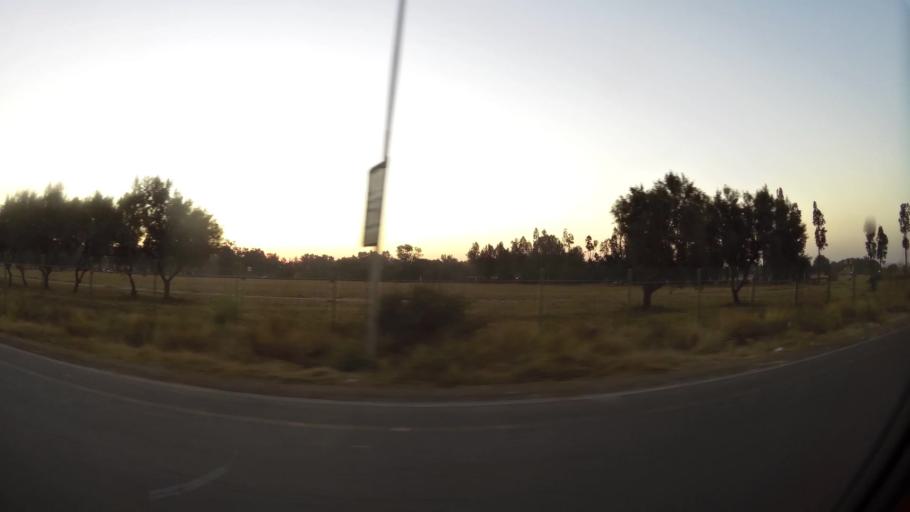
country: ZA
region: North-West
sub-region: Bojanala Platinum District Municipality
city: Rustenburg
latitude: -25.6426
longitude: 27.2615
